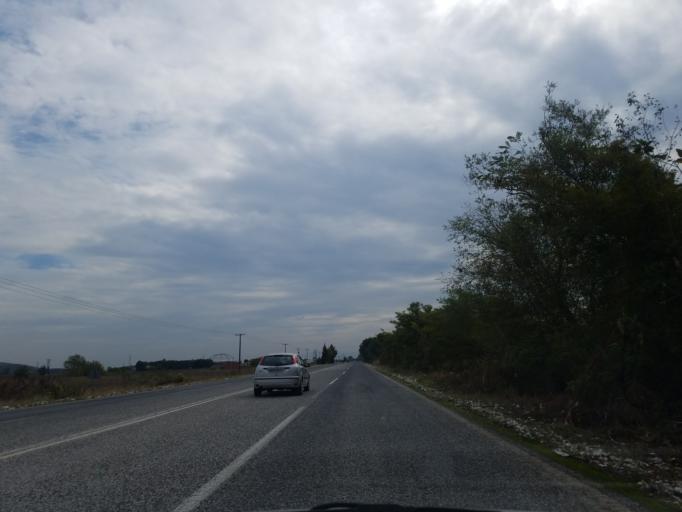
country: GR
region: Thessaly
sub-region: Nomos Kardhitsas
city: Karpochori
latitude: 39.3647
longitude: 22.0319
